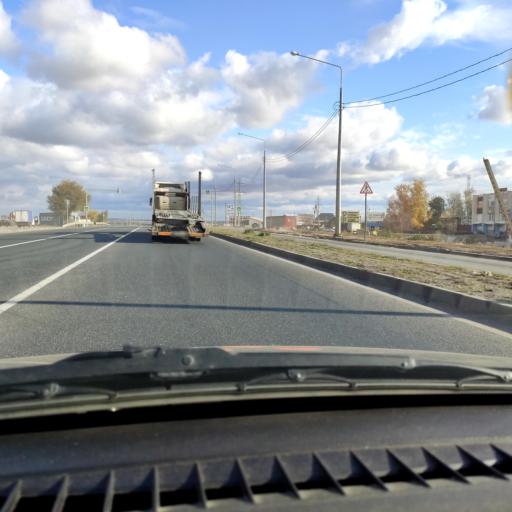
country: RU
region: Samara
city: Varlamovo
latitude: 53.1935
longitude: 48.3621
